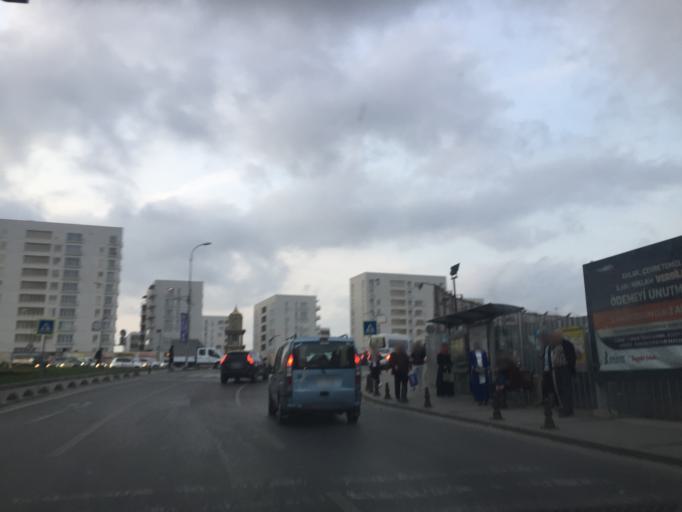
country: TR
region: Istanbul
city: Samandira
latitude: 40.9898
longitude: 29.2296
